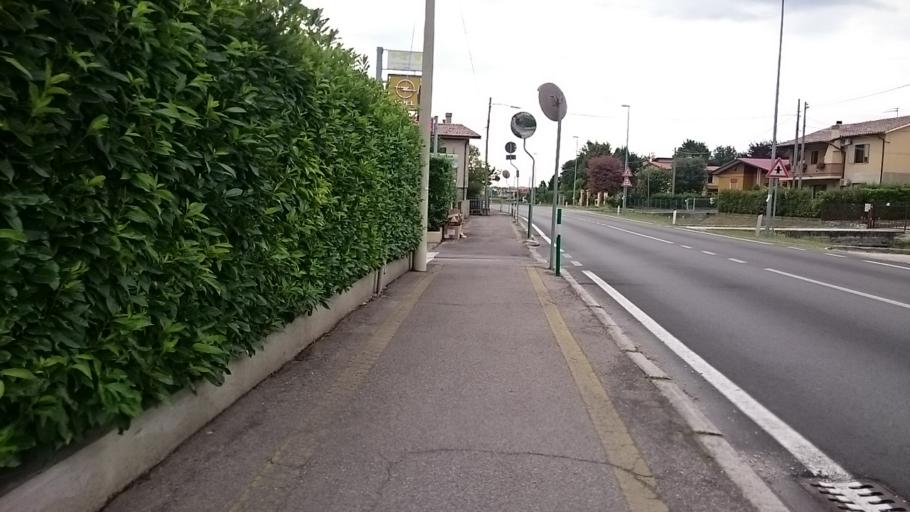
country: IT
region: Veneto
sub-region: Provincia di Padova
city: Masera di Padova
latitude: 45.3185
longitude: 11.8716
